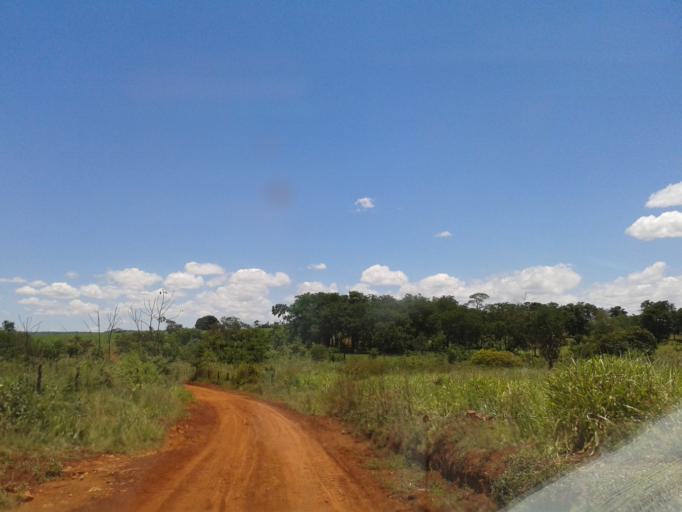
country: BR
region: Minas Gerais
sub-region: Centralina
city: Centralina
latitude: -18.6650
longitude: -49.2379
